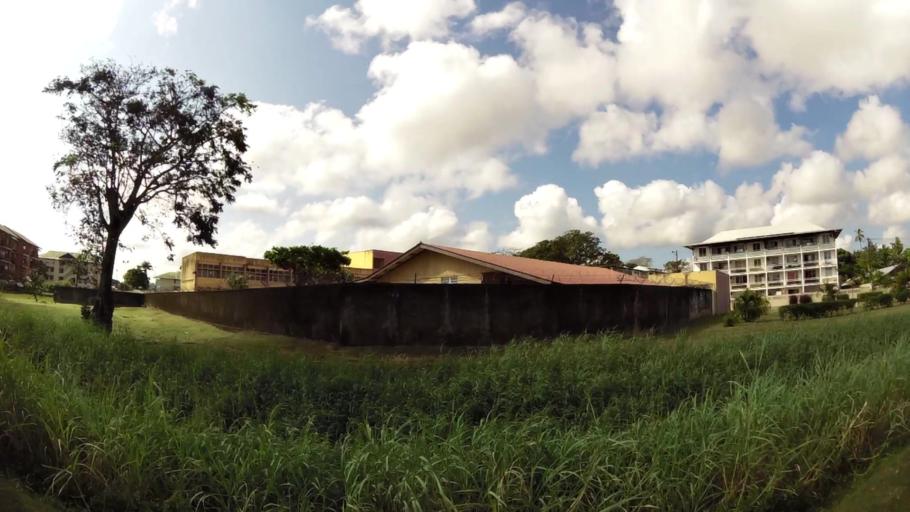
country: GF
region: Guyane
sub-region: Guyane
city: Cayenne
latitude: 4.9350
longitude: -52.3177
